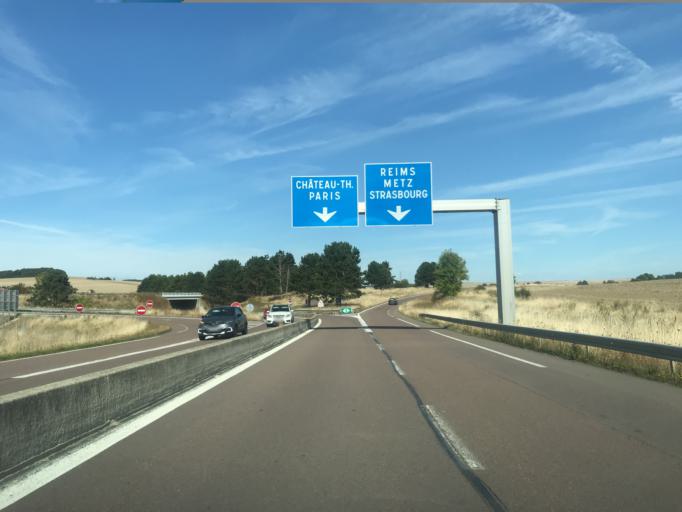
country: FR
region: Champagne-Ardenne
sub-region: Departement de la Marne
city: Chatillon-sur-Marne
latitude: 49.1548
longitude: 3.7181
